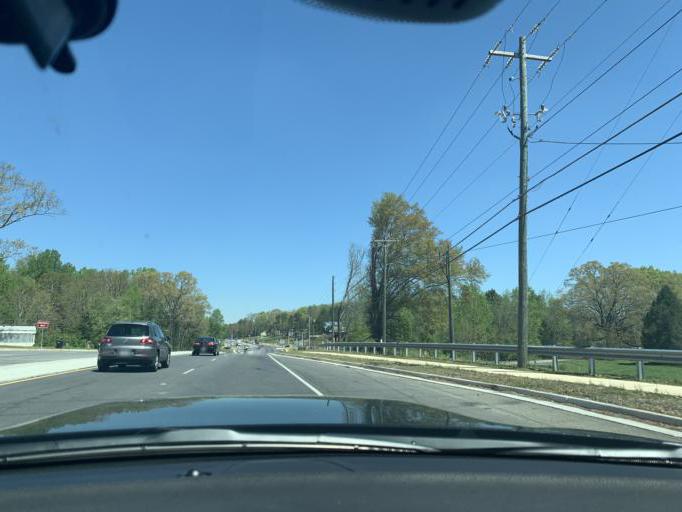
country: US
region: Georgia
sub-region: Forsyth County
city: Cumming
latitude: 34.1971
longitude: -84.1971
